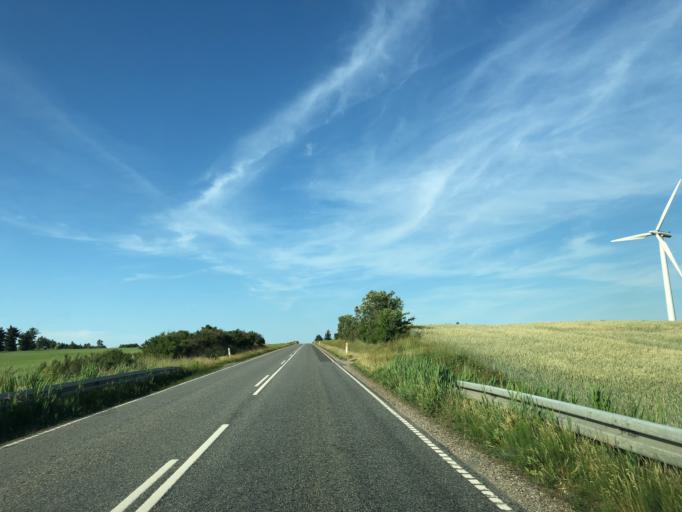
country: DK
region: Central Jutland
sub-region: Struer Kommune
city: Struer
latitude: 56.4236
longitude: 8.5047
